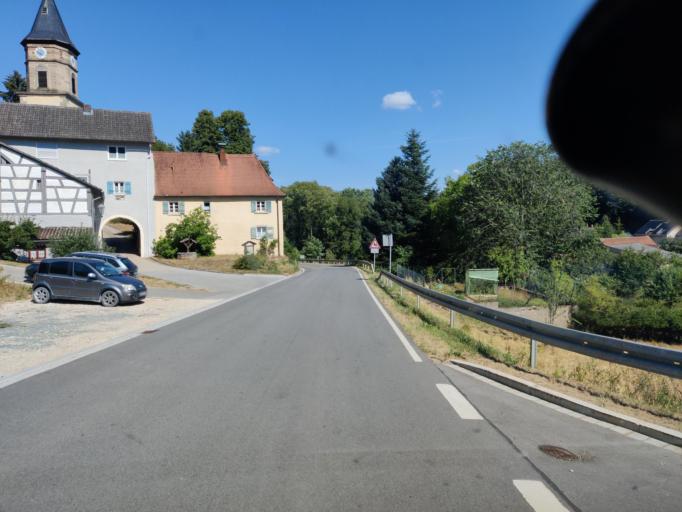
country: DE
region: Bavaria
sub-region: Regierungsbezirk Mittelfranken
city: Bergen
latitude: 49.0711
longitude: 11.0849
